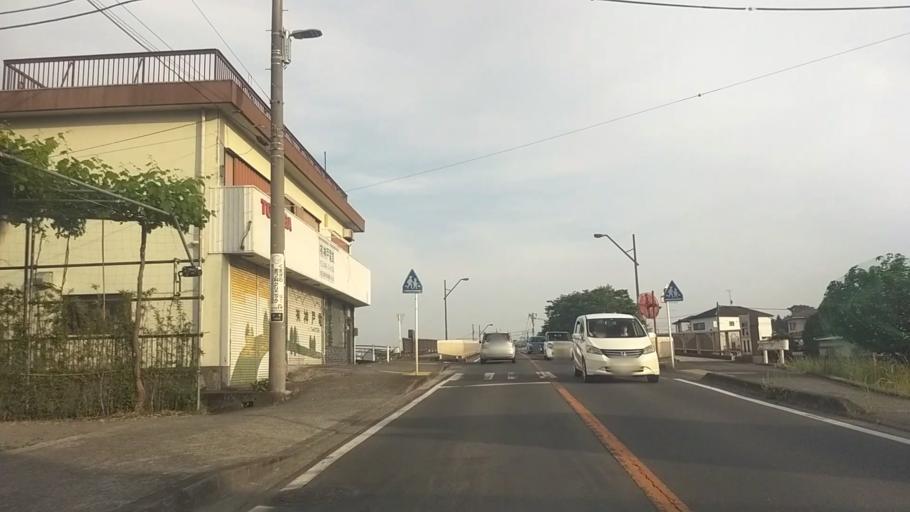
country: JP
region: Kanagawa
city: Odawara
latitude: 35.3045
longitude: 139.1244
